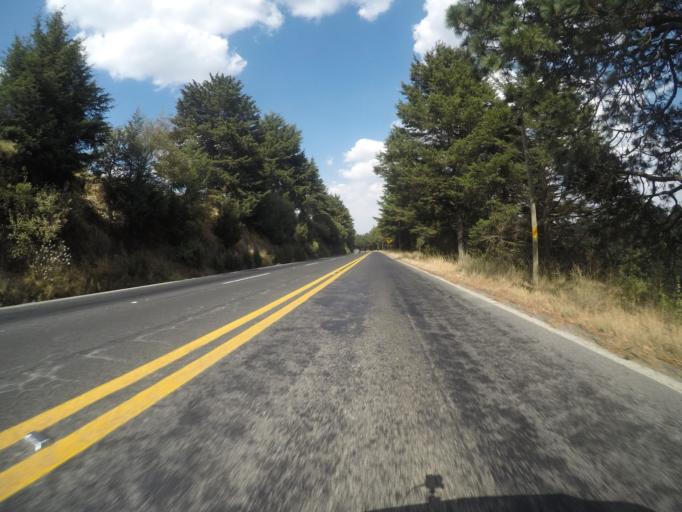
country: MX
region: Mexico
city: Cerro La Calera
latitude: 19.2203
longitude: -99.7969
